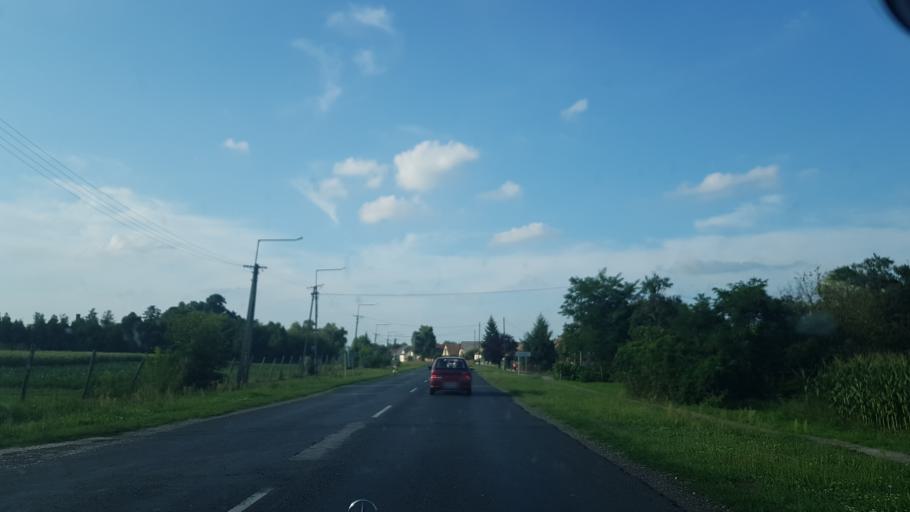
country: HU
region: Somogy
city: Nagyatad
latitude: 46.2802
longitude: 17.3610
